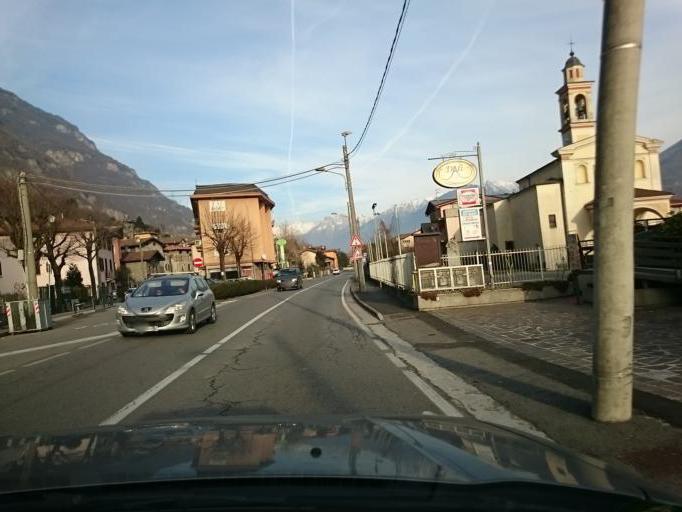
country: IT
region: Lombardy
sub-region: Provincia di Brescia
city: Sacca
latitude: 45.9068
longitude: 10.2026
